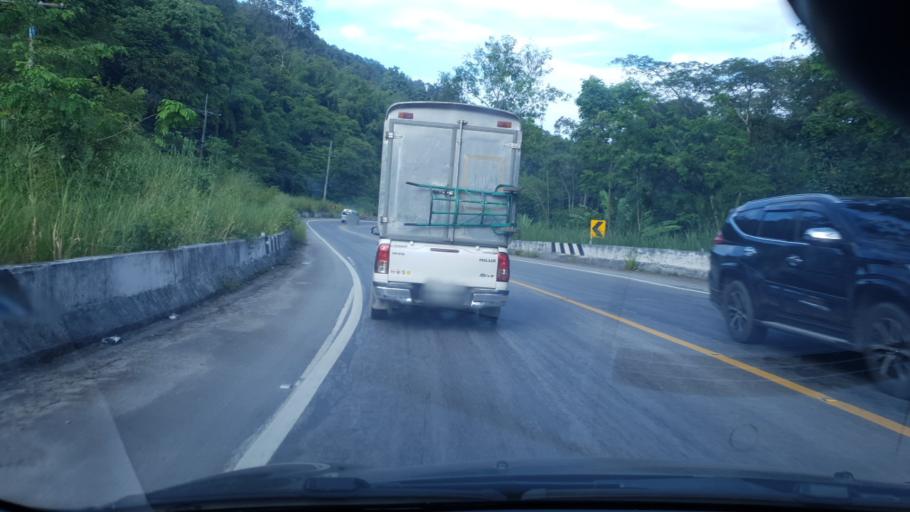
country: TH
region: Lampang
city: Wang Nuea
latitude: 19.0916
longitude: 99.4211
